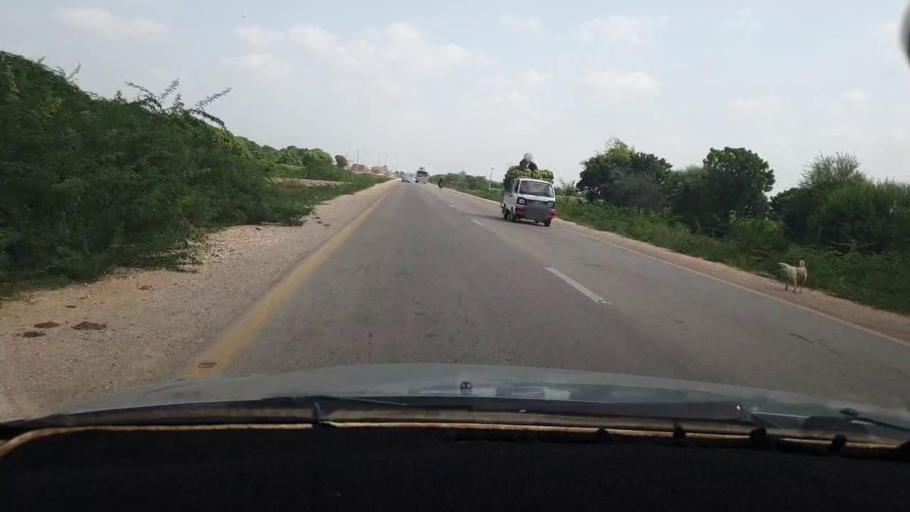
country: PK
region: Sindh
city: Digri
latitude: 25.0908
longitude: 69.1945
